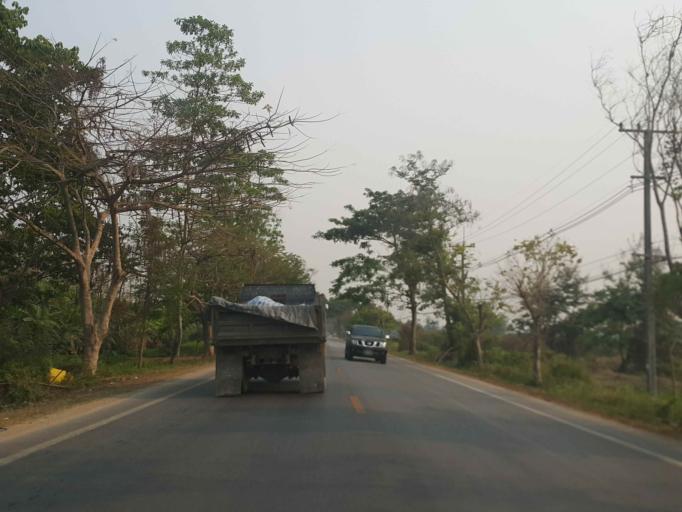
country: TH
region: Chiang Mai
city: Mae Taeng
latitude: 19.0216
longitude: 98.9691
